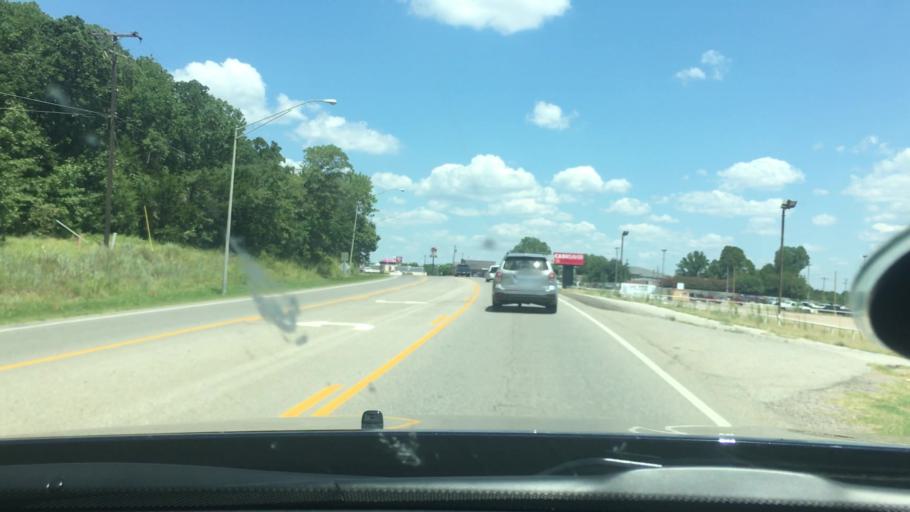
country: US
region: Oklahoma
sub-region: Marshall County
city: Madill
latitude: 34.0769
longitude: -96.7631
